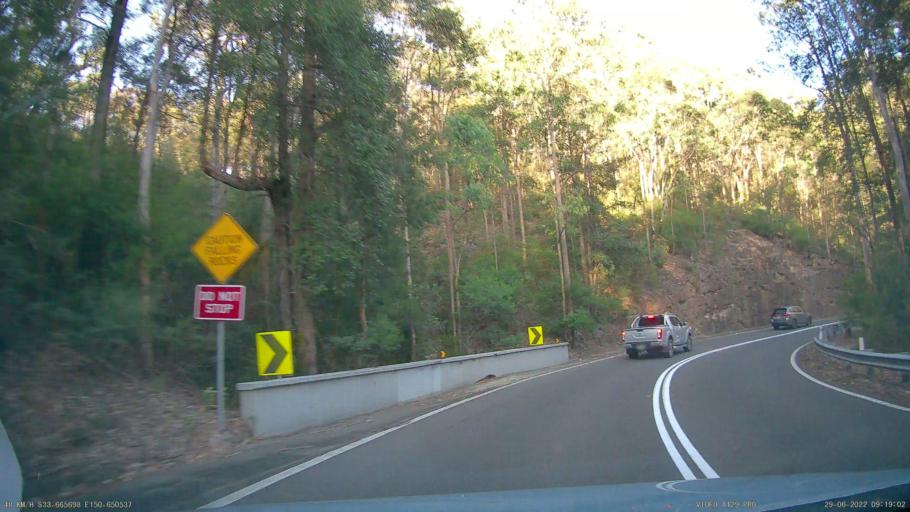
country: AU
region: New South Wales
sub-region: Penrith Municipality
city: Emu Heights
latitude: -33.6660
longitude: 150.6503
